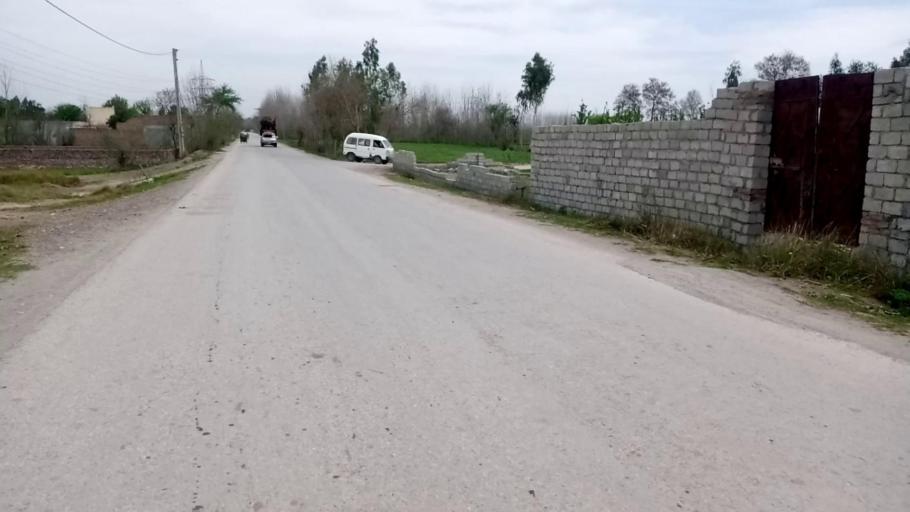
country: PK
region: Khyber Pakhtunkhwa
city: Charsadda
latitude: 34.0633
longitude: 71.6912
